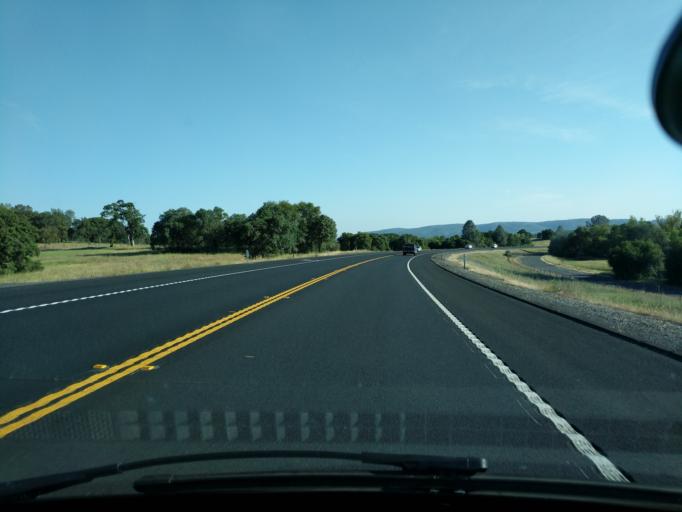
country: US
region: California
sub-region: Calaveras County
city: Copperopolis
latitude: 37.9817
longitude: -120.6455
